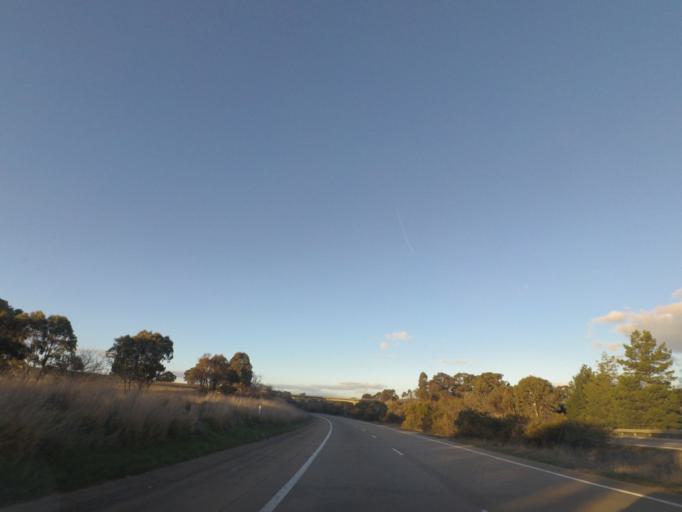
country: AU
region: New South Wales
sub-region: Yass Valley
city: Yass
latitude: -34.8088
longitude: 148.9015
